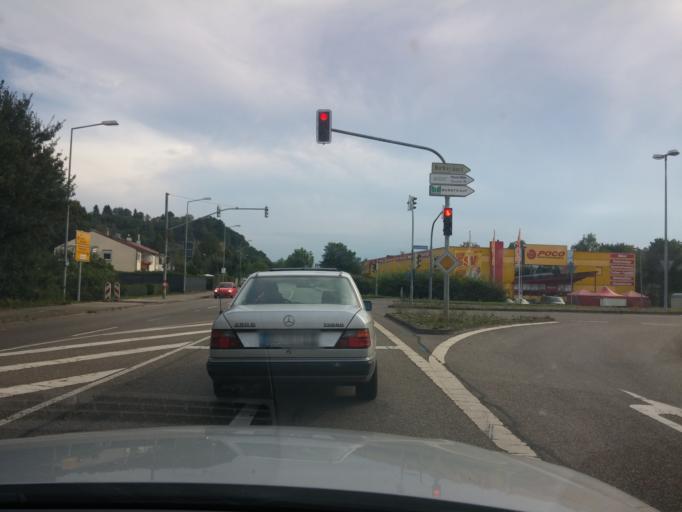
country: DE
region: Baden-Wuerttemberg
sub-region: Tuebingen Region
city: Warthausen
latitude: 48.1139
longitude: 9.8044
